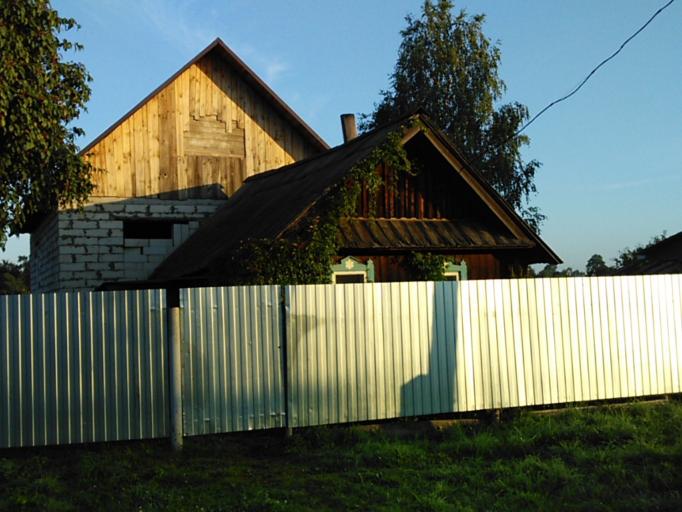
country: RU
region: Perm
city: Foki
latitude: 56.6878
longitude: 54.3432
